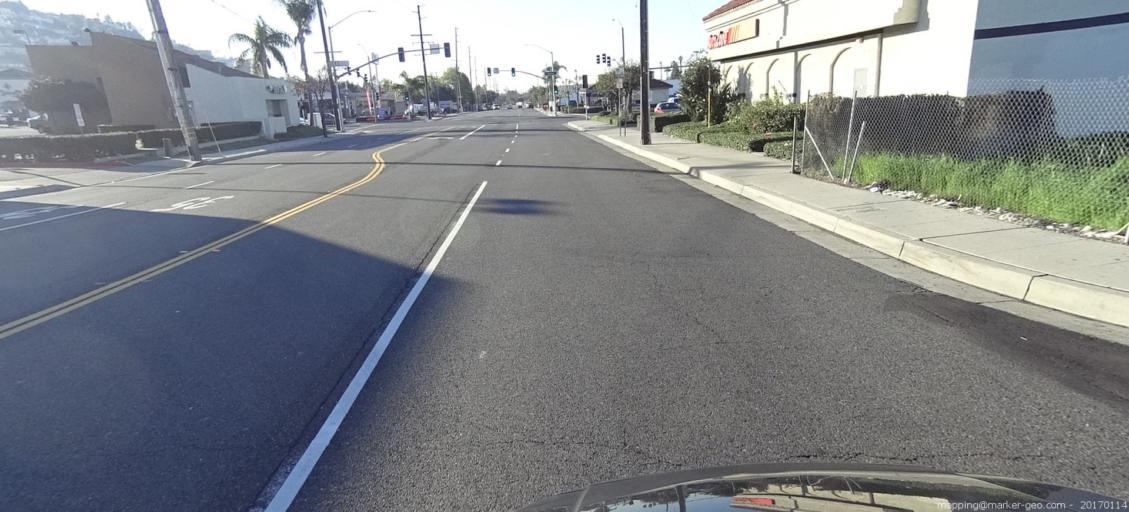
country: US
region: California
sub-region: Orange County
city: Villa Park
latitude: 33.7887
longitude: -117.8058
